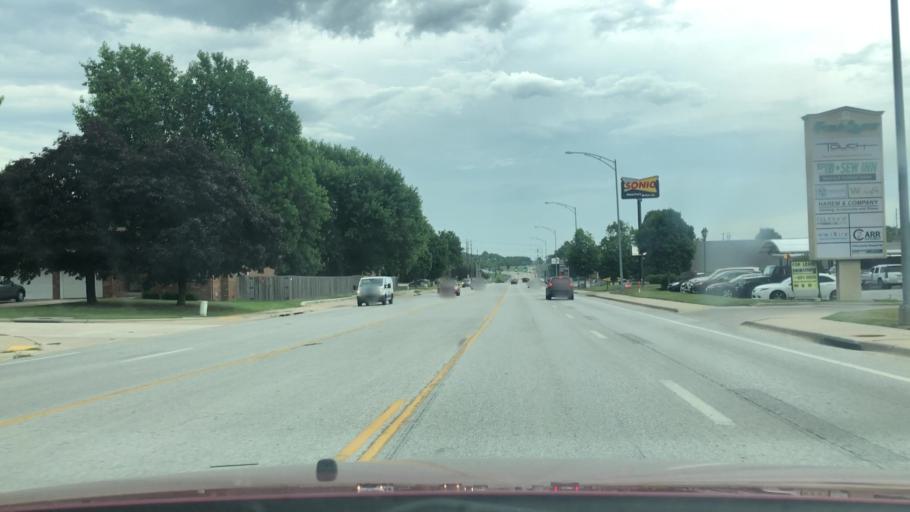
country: US
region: Missouri
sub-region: Greene County
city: Springfield
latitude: 37.1374
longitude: -93.2667
